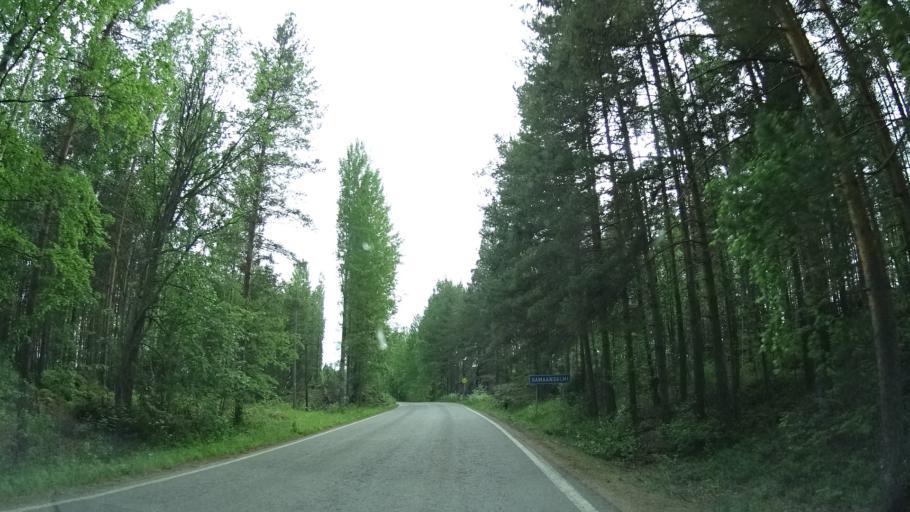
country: FI
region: Central Finland
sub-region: Joutsa
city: Luhanka
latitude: 61.6717
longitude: 25.6266
